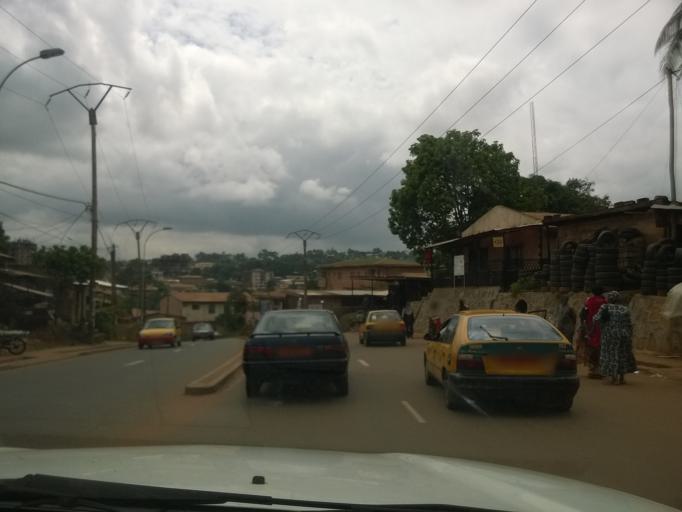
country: CM
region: Centre
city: Yaounde
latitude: 3.8360
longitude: 11.4960
